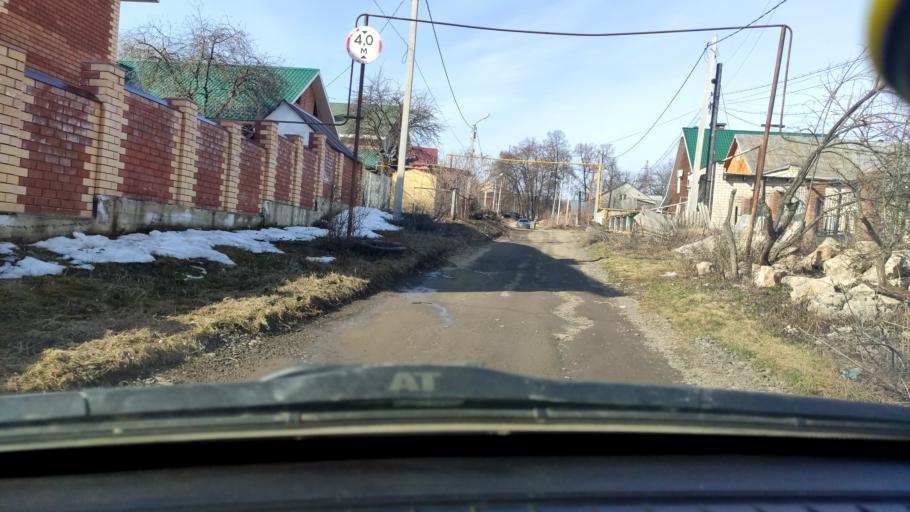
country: RU
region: Samara
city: Zhigulevsk
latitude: 53.3909
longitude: 49.4939
